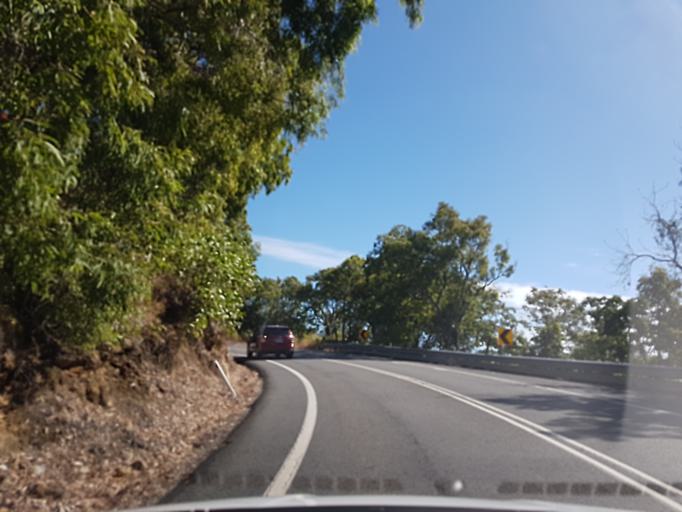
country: AU
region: Queensland
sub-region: Cairns
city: Port Douglas
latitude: -16.6205
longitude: 145.5438
